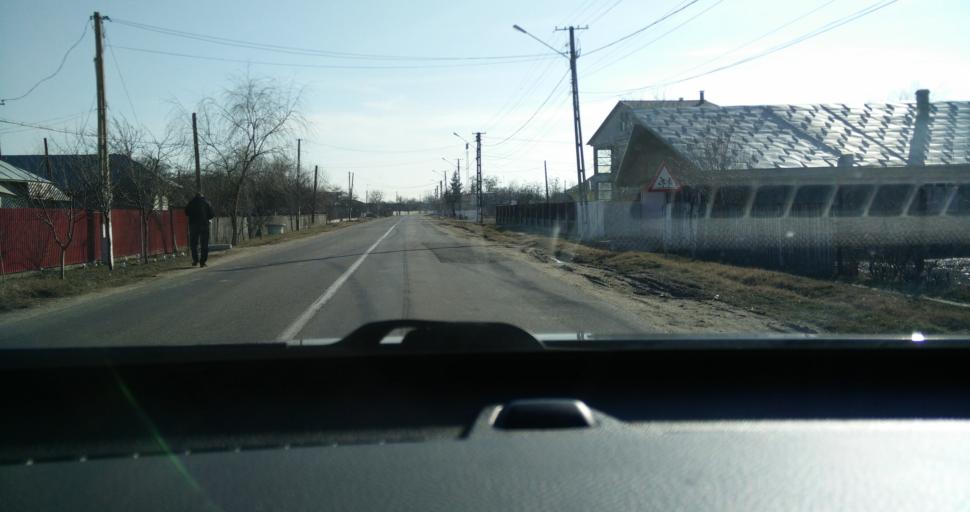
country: RO
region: Vrancea
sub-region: Comuna Nanesti
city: Nanesti
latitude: 45.5465
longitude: 27.4992
